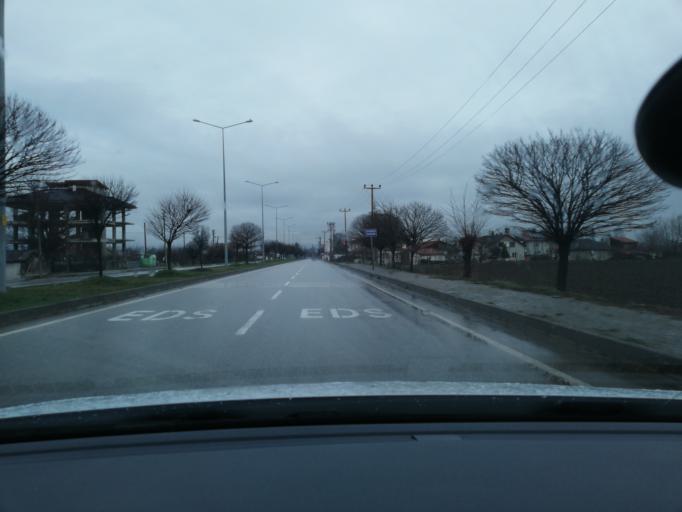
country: TR
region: Bolu
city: Bolu
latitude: 40.7012
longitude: 31.6183
